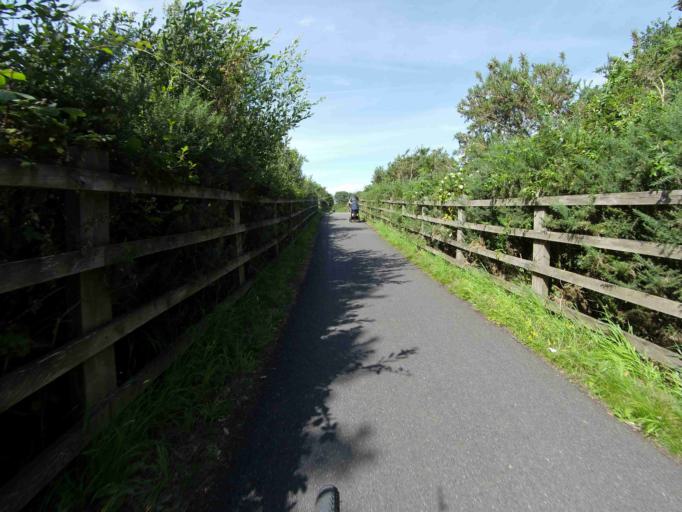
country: GB
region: England
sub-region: Devon
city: Topsham
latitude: 50.6763
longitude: -3.4497
